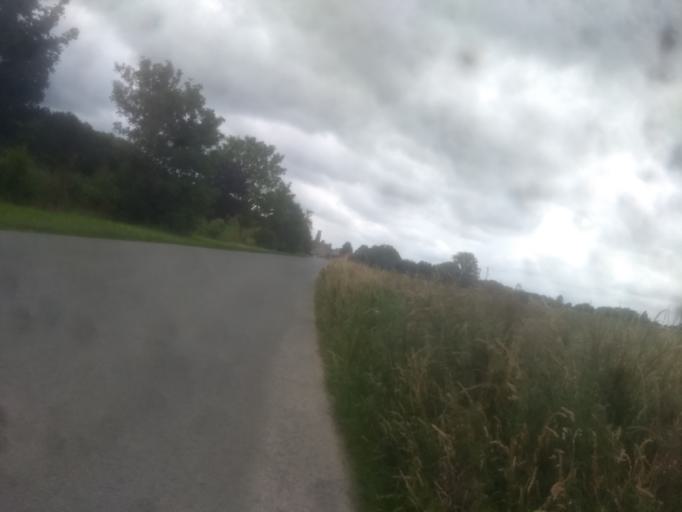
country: FR
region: Nord-Pas-de-Calais
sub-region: Departement du Pas-de-Calais
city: Thelus
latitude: 50.3308
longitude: 2.7930
